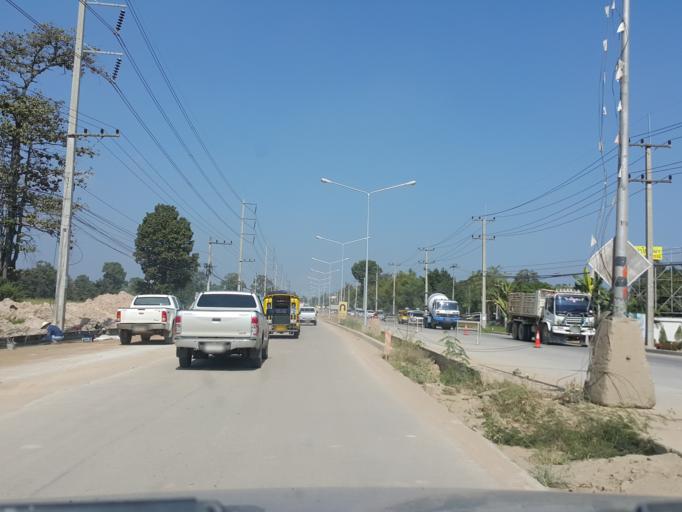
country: TH
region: Chiang Mai
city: Chiang Mai
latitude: 18.8718
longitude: 98.9632
